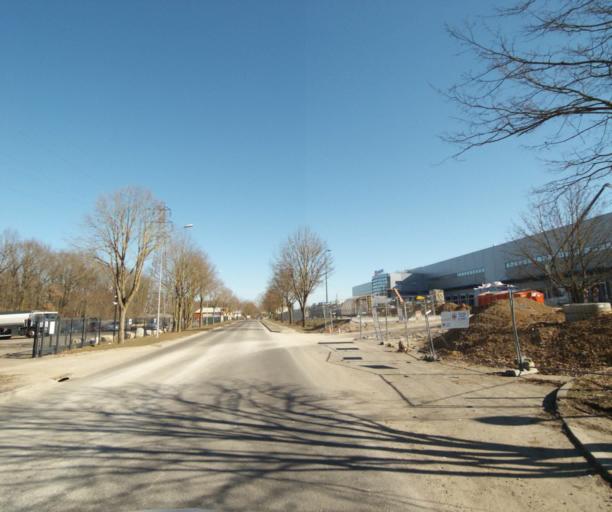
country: FR
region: Lorraine
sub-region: Departement de Meurthe-et-Moselle
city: Fleville-devant-Nancy
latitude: 48.6108
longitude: 6.1937
